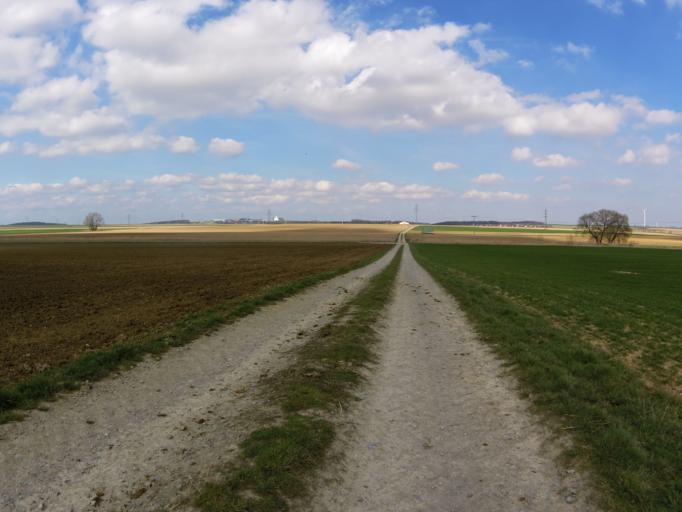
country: DE
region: Bavaria
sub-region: Regierungsbezirk Unterfranken
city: Biebelried
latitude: 49.7475
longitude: 10.0802
